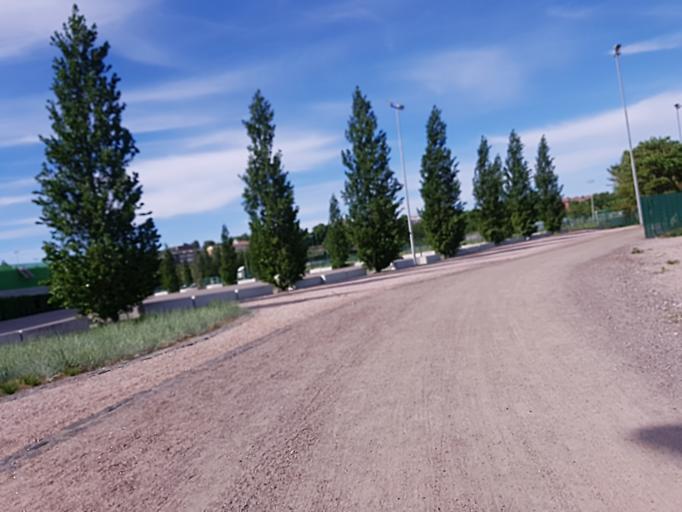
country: FI
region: Uusimaa
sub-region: Helsinki
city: Helsinki
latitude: 60.2036
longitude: 24.9400
